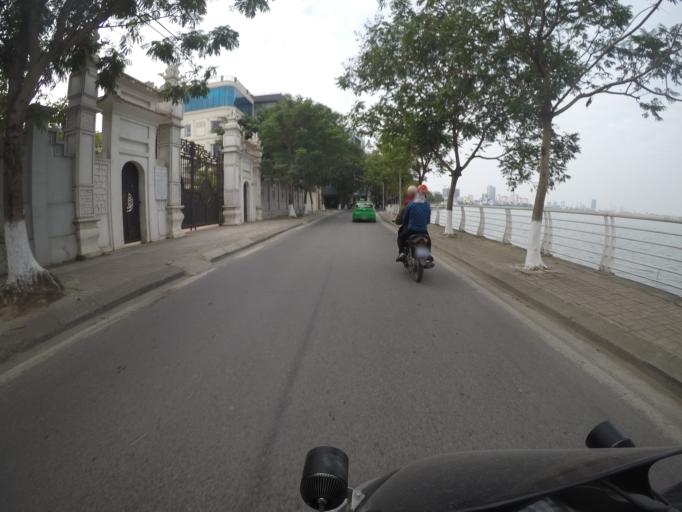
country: VN
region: Ha Noi
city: Tay Ho
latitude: 21.0534
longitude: 105.8124
